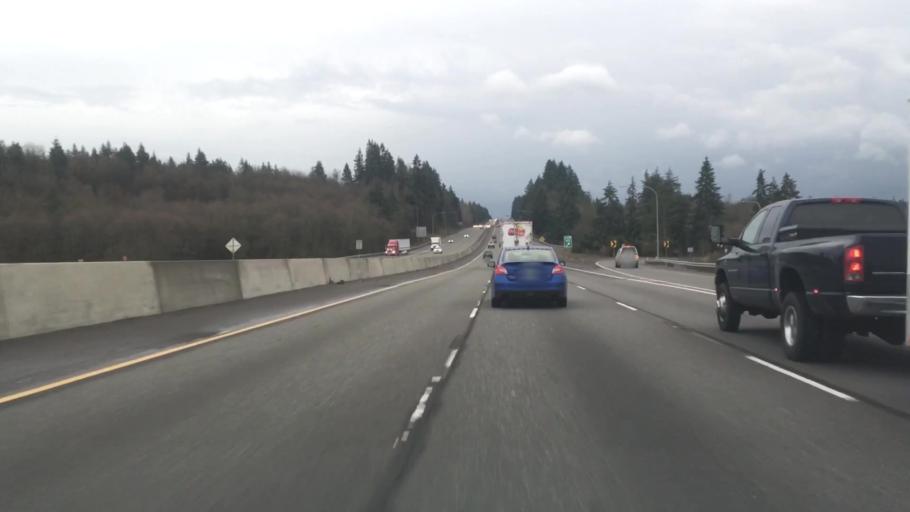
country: US
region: Washington
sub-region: Thurston County
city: Tenino
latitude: 46.8960
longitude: -122.9611
